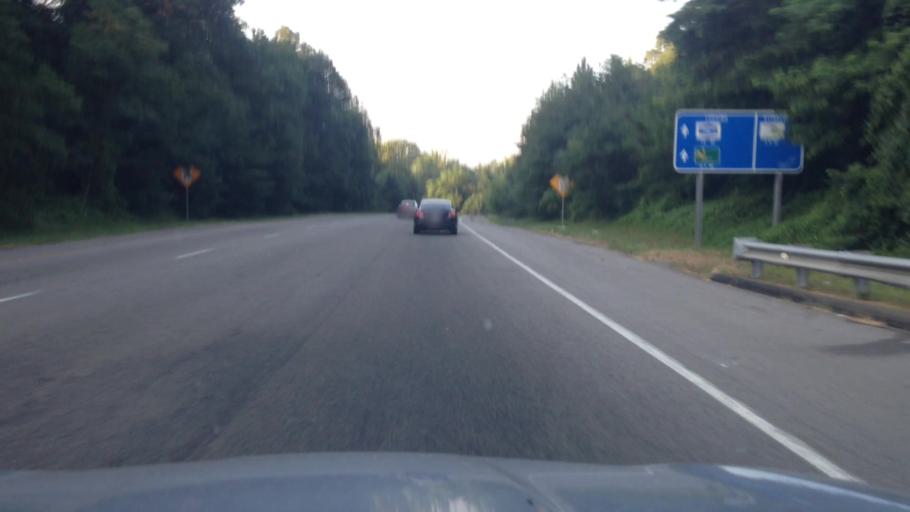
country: US
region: Virginia
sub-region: Prince William County
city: Woodbridge
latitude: 38.6757
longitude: -77.2337
